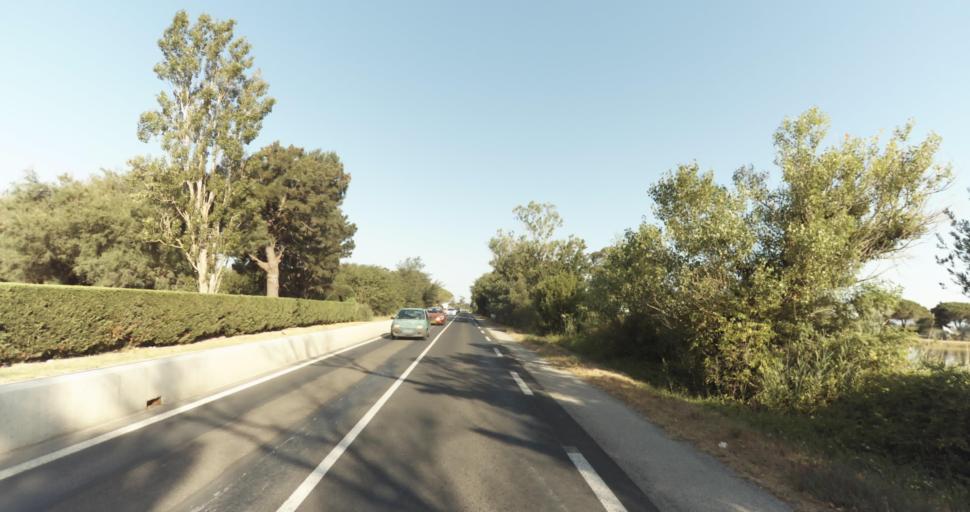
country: FR
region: Languedoc-Roussillon
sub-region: Departement des Pyrenees-Orientales
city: Saint-Cyprien-Plage
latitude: 42.6386
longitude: 3.0217
